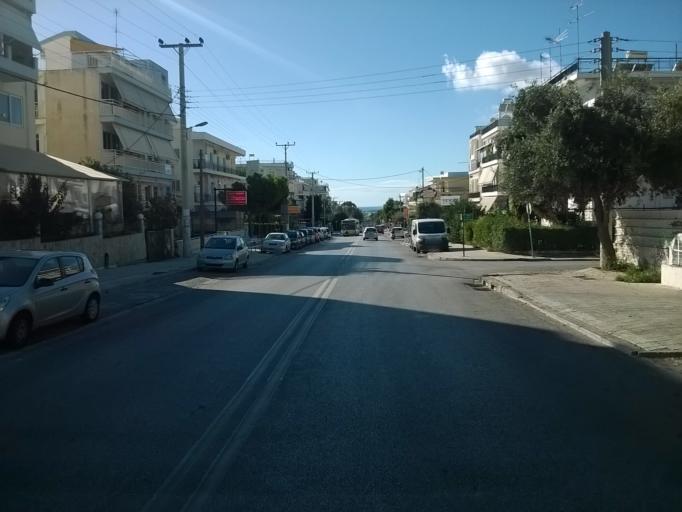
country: GR
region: Attica
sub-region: Nomarchia Athinas
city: Glyfada
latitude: 37.8822
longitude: 23.7591
